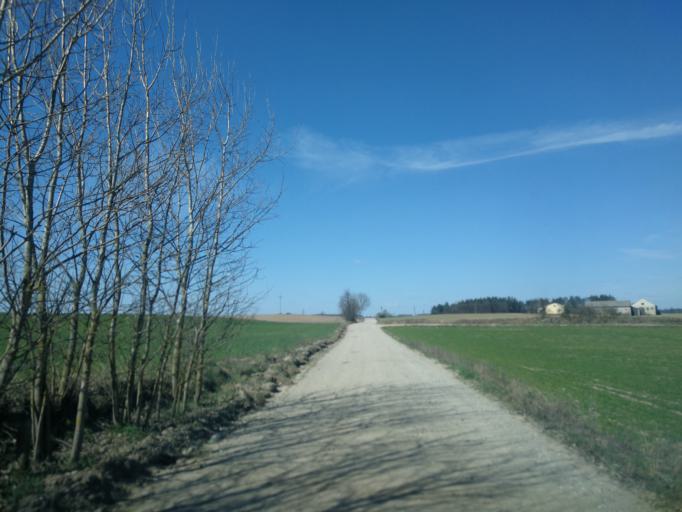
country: PL
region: Warmian-Masurian Voivodeship
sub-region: Powiat dzialdowski
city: Rybno
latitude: 53.4413
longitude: 19.9367
